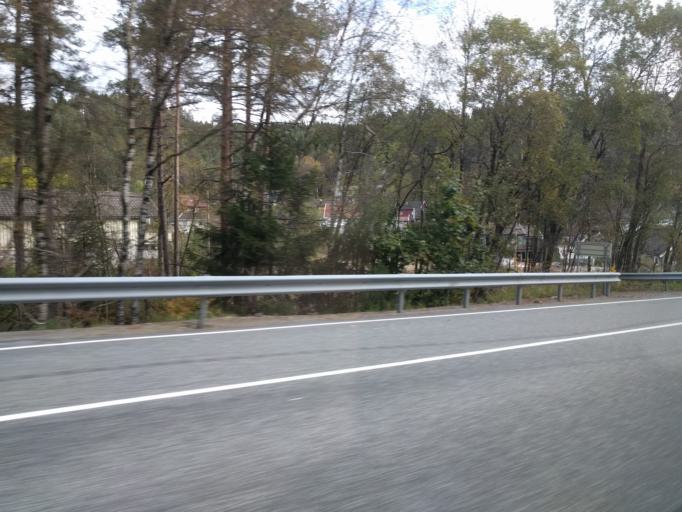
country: NO
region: Vest-Agder
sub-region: Songdalen
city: Nodeland
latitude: 58.2971
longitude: 7.8313
